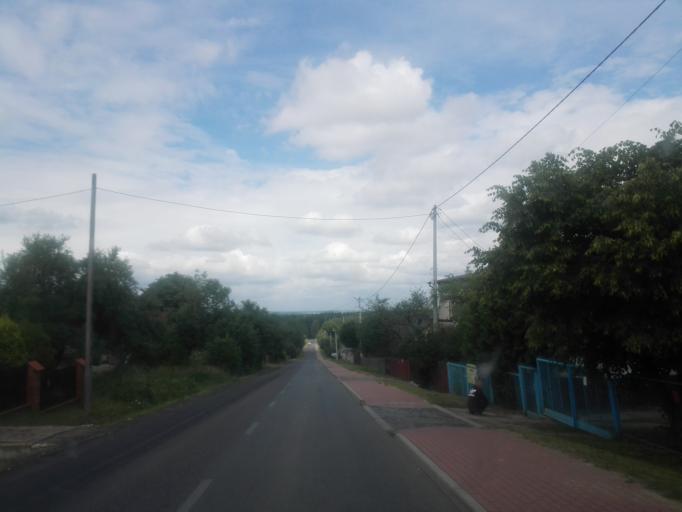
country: PL
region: Silesian Voivodeship
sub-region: Powiat myszkowski
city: Choron
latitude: 50.7116
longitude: 19.2668
